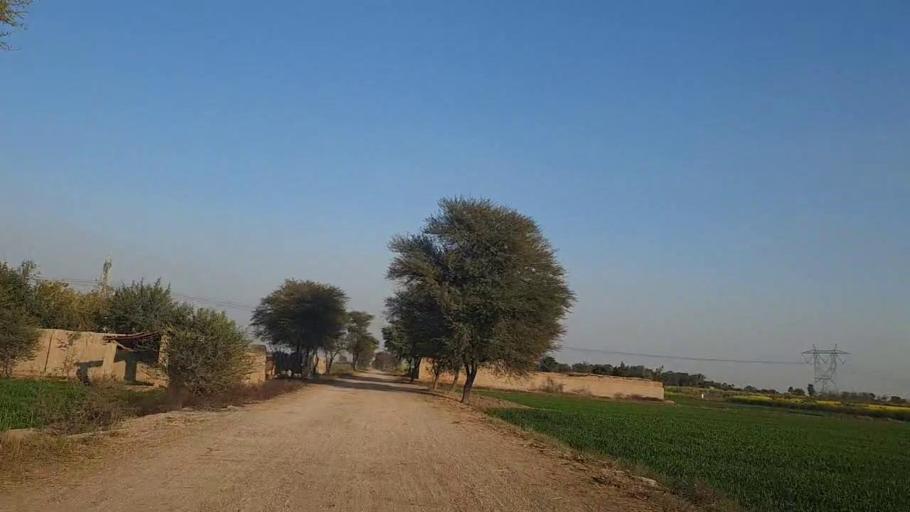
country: PK
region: Sindh
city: Sakrand
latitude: 26.3052
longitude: 68.1484
